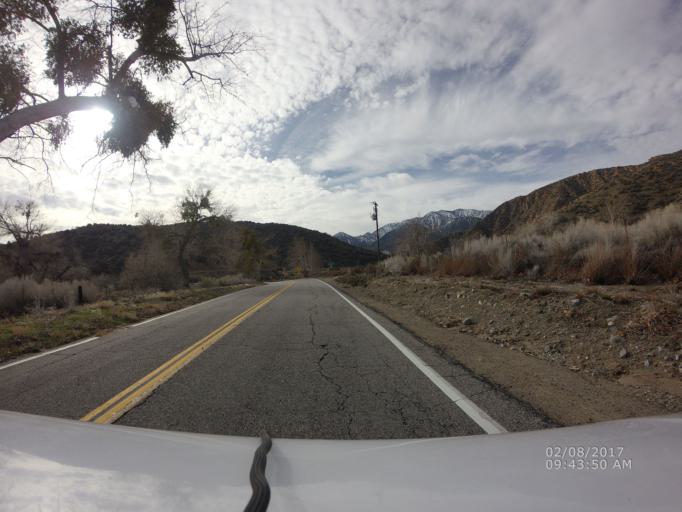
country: US
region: California
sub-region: Los Angeles County
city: Littlerock
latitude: 34.4333
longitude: -117.8353
